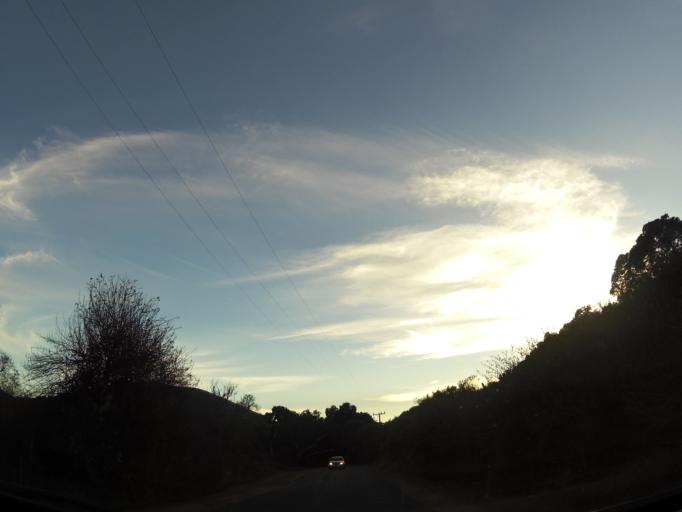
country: US
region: California
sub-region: Monterey County
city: Prunedale
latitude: 36.7819
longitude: -121.5929
